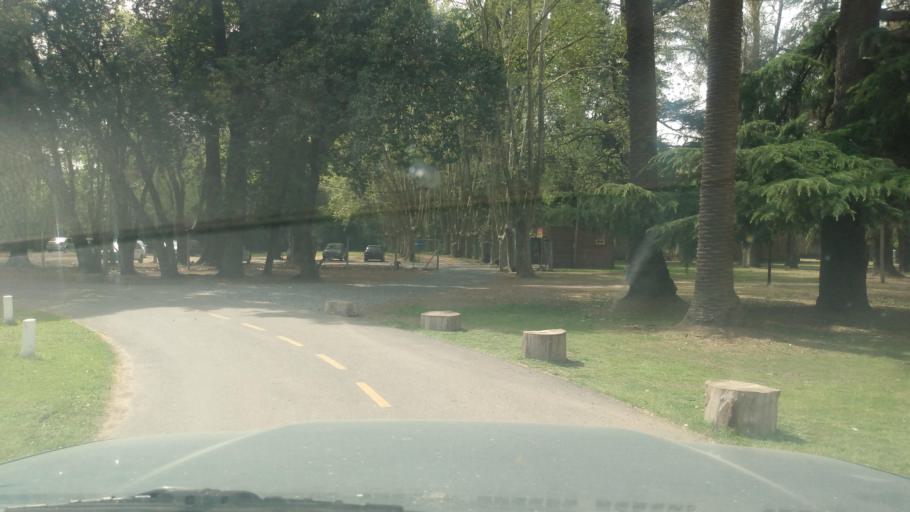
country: AR
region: Buenos Aires
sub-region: Partido de Pilar
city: Pilar
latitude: -34.4381
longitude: -58.8921
